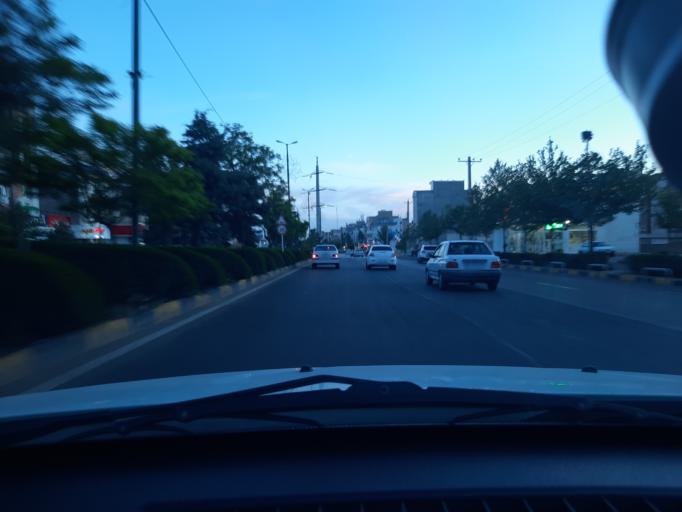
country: IR
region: Qazvin
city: Qazvin
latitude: 36.3068
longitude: 50.0119
